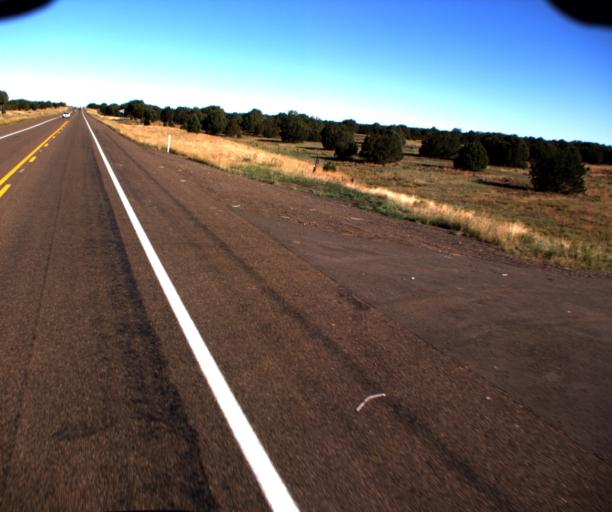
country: US
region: Arizona
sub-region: Navajo County
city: Show Low
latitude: 34.2873
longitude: -110.0298
